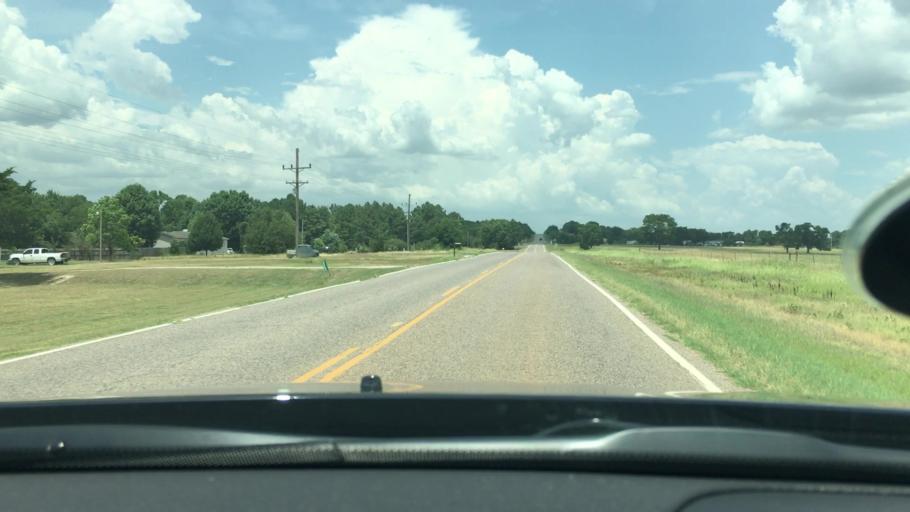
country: US
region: Oklahoma
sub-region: Marshall County
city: Oakland
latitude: 33.9922
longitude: -96.8821
